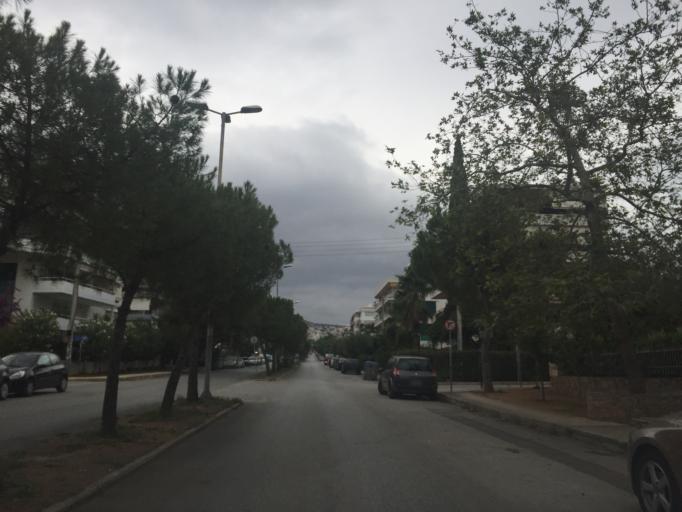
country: GR
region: Attica
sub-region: Nomarchia Athinas
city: Glyfada
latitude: 37.8538
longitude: 23.7580
